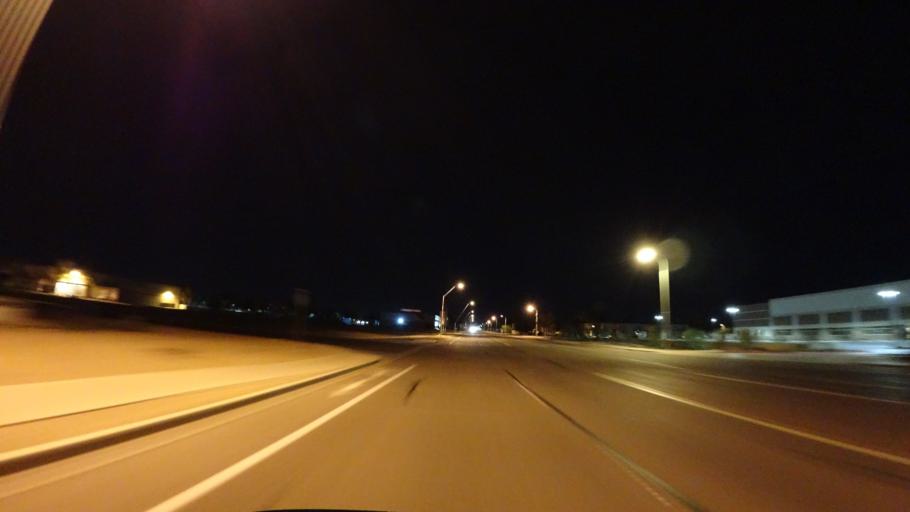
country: US
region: Arizona
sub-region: Maricopa County
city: San Carlos
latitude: 33.3498
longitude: -111.8399
